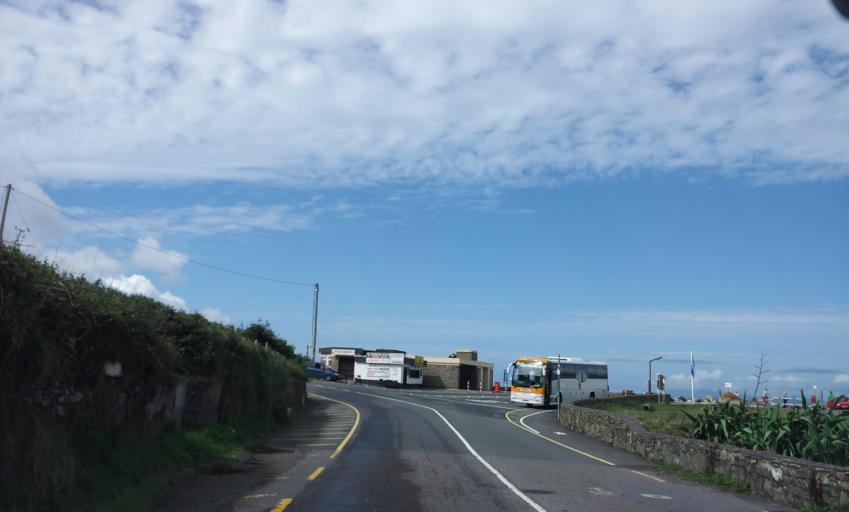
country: IE
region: Munster
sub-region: Ciarrai
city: Killorglin
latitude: 52.0541
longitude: -9.9753
